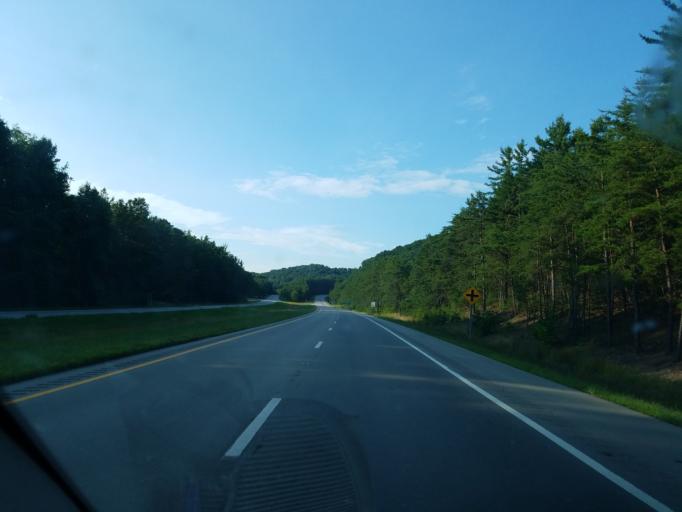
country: US
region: Ohio
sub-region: Adams County
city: Peebles
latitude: 39.0050
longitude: -83.2969
